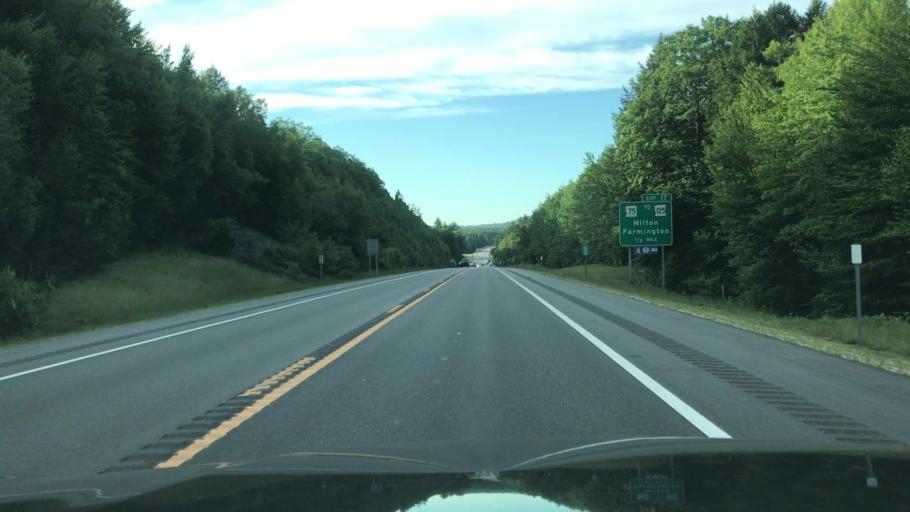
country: US
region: New Hampshire
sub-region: Strafford County
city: Farmington
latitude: 43.3926
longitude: -71.0012
